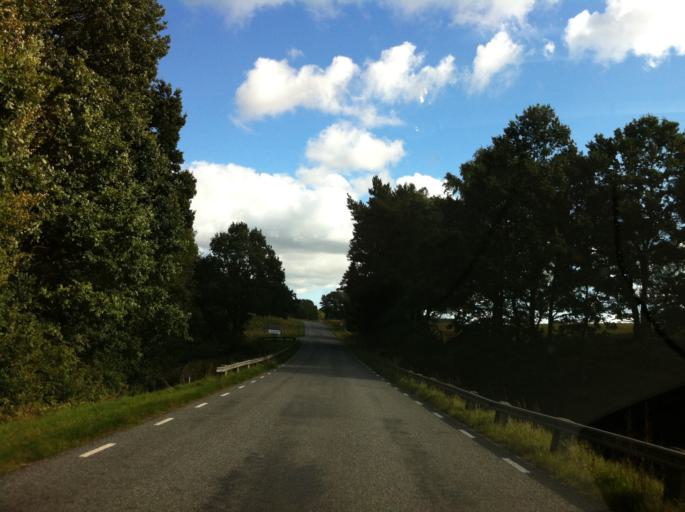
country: SE
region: Skane
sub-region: Kristianstads Kommun
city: Degeberga
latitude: 55.7120
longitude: 13.9804
